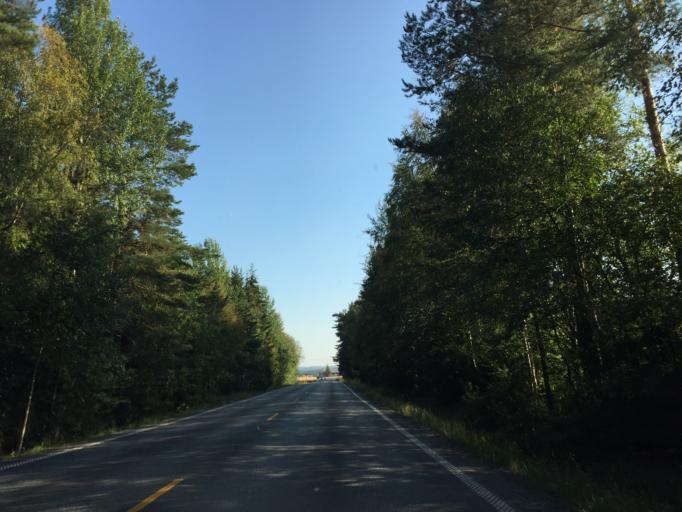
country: NO
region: Akershus
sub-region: Nes
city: Arnes
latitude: 60.1417
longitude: 11.4899
